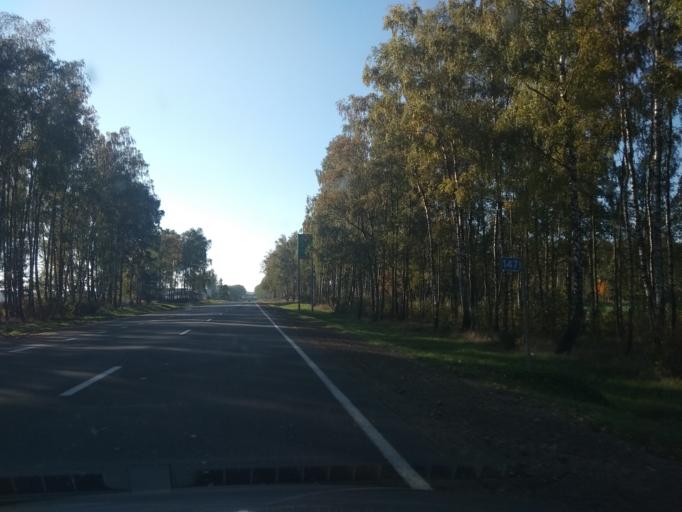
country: BY
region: Grodnenskaya
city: Vyalikaya Byerastavitsa
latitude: 53.1175
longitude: 24.0080
